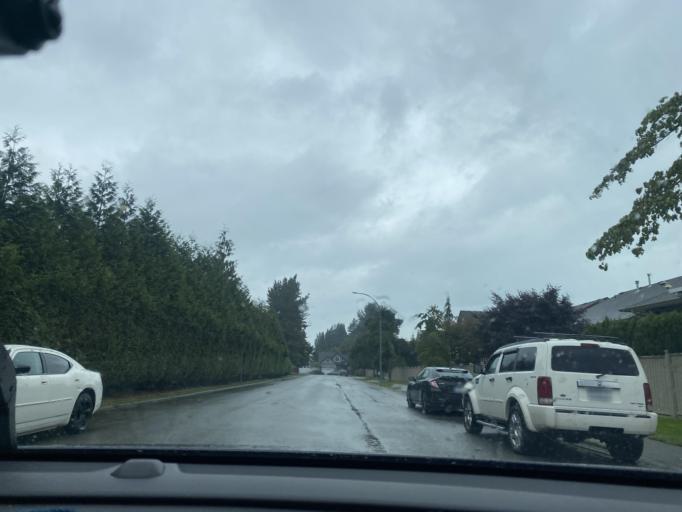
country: CA
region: British Columbia
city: Agassiz
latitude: 49.2987
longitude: -121.7833
